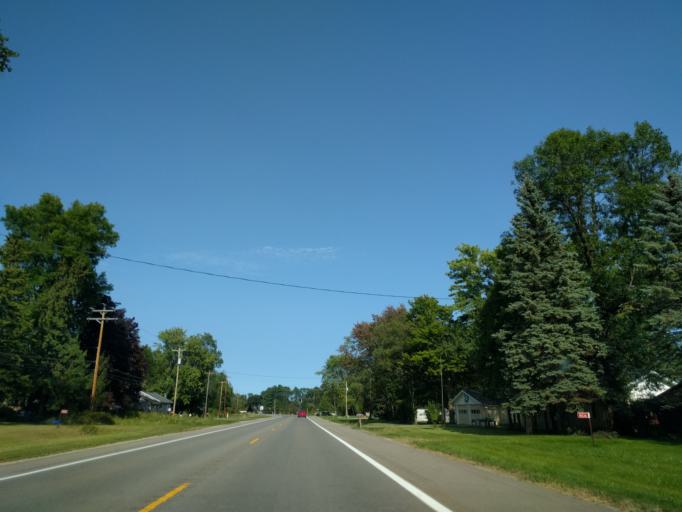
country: US
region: Michigan
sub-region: Menominee County
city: Menominee
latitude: 45.1716
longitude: -87.5784
